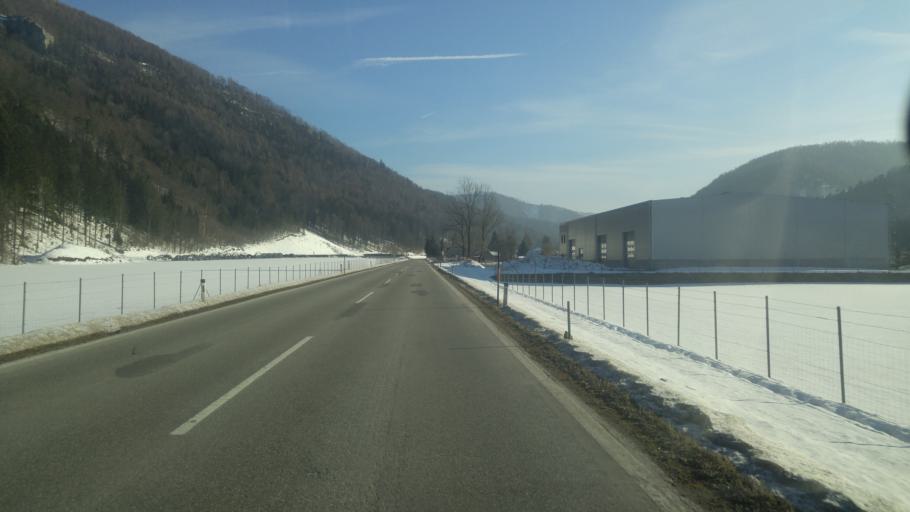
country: AT
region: Lower Austria
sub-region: Politischer Bezirk Lilienfeld
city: Hohenberg
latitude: 47.9326
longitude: 15.6049
